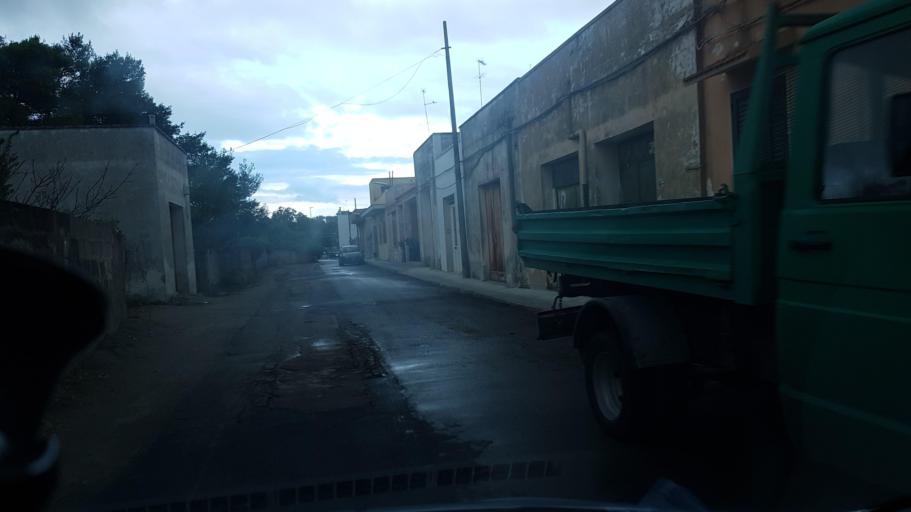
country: IT
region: Apulia
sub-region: Provincia di Lecce
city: Novoli
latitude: 40.3661
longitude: 18.0712
